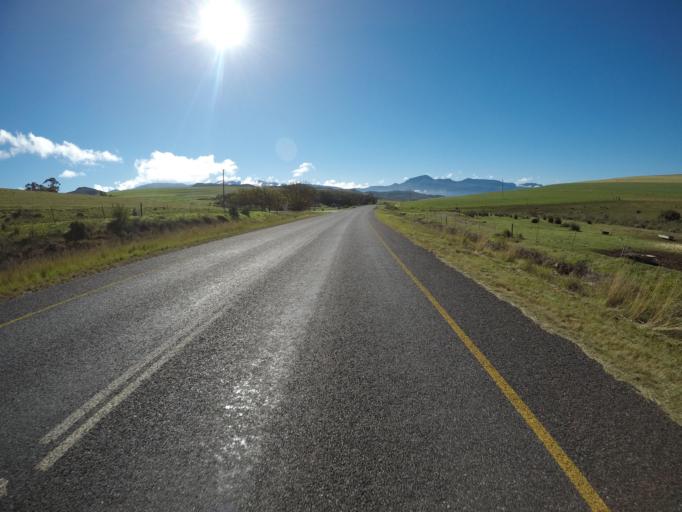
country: ZA
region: Western Cape
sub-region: Overberg District Municipality
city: Caledon
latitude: -34.1261
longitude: 19.5140
